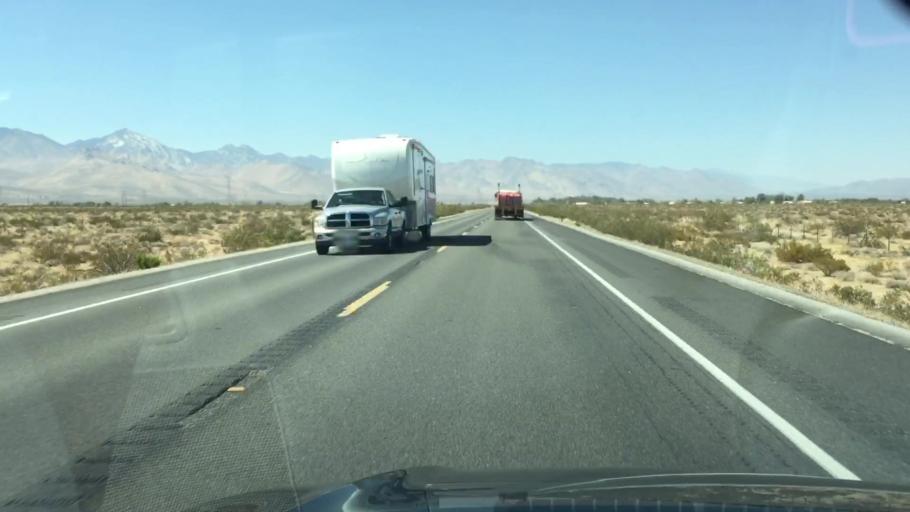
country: US
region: California
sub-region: Kern County
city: China Lake Acres
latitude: 35.6243
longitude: -117.7771
